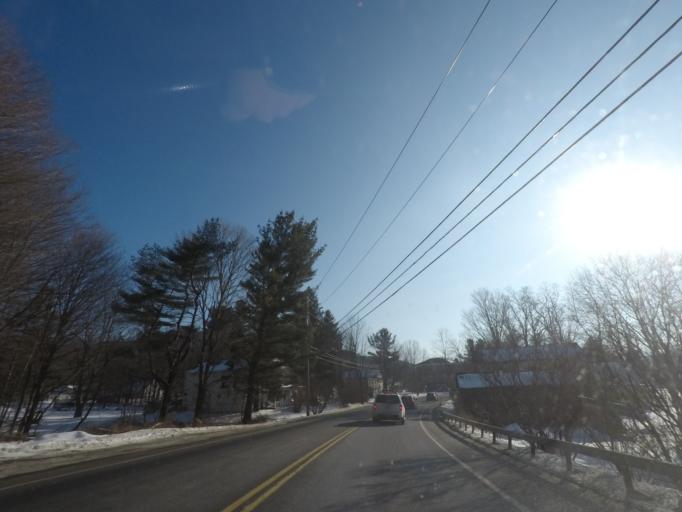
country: US
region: Massachusetts
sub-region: Berkshire County
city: Richmond
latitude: 42.4801
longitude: -73.3730
